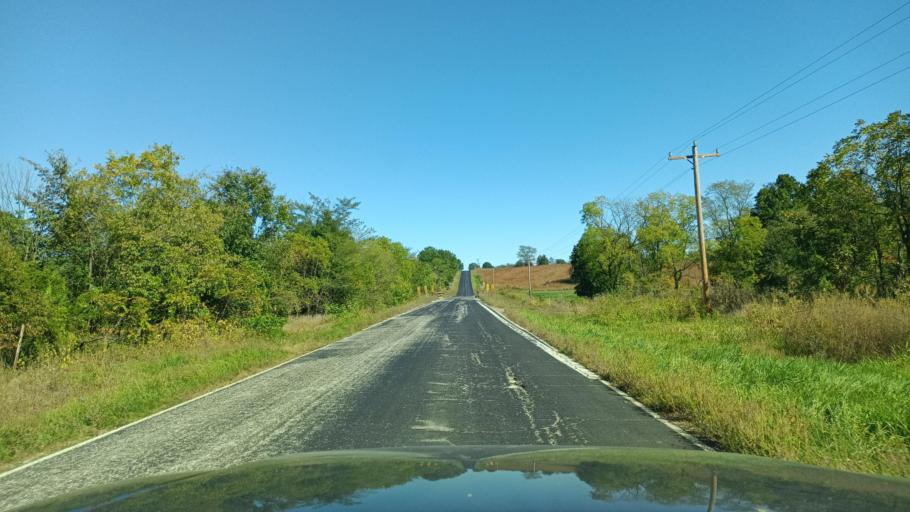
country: US
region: Missouri
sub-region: Macon County
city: La Plata
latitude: 39.9284
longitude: -92.5828
